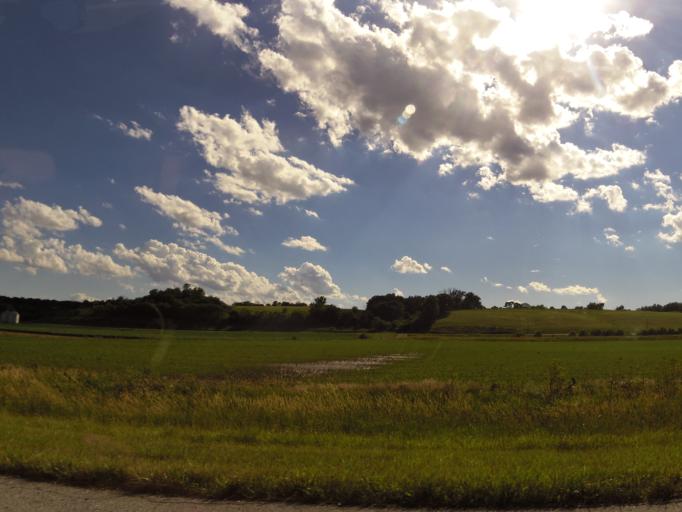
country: US
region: Illinois
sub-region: Adams County
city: Quincy
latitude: 39.9731
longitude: -91.5209
